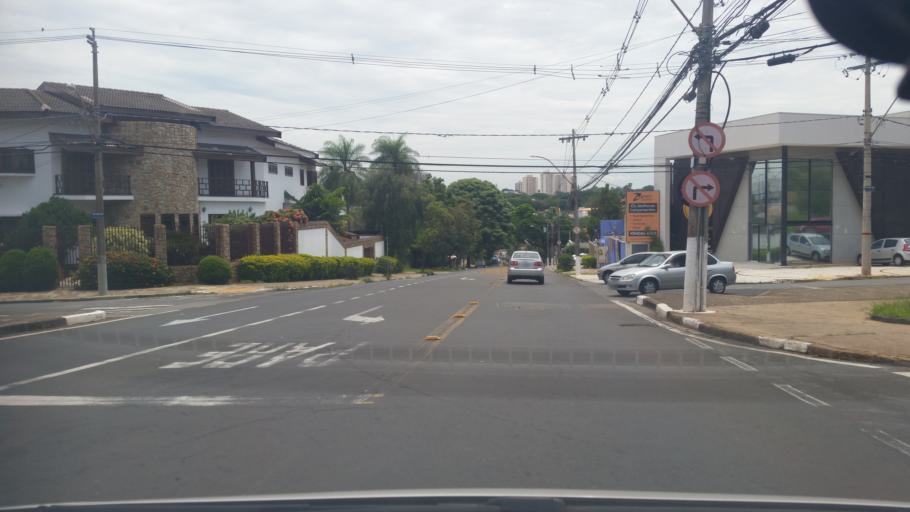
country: BR
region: Sao Paulo
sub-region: Campinas
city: Campinas
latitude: -22.8698
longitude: -47.0591
